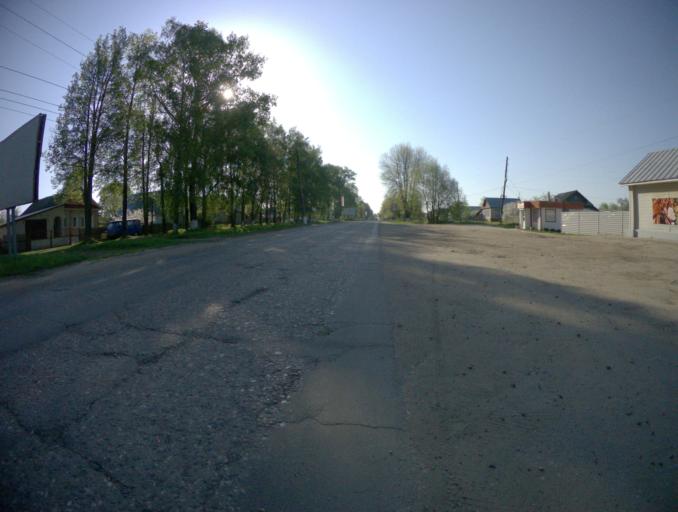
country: RU
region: Vladimir
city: Vyazniki
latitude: 56.2371
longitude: 42.1786
